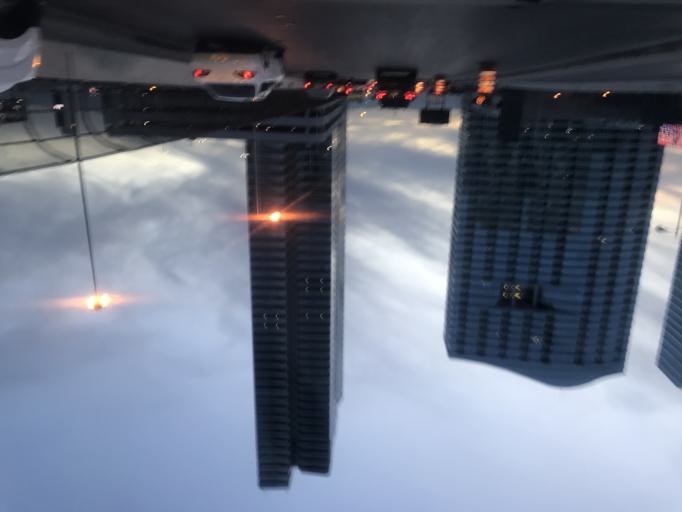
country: US
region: Nevada
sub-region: Clark County
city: Paradise
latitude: 36.1082
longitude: -115.1799
